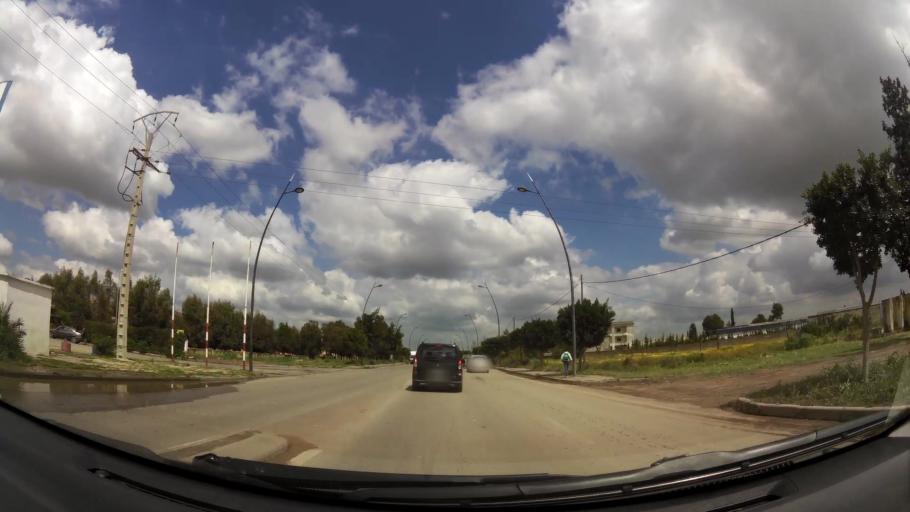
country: MA
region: Chaouia-Ouardigha
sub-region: Settat Province
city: Berrechid
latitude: 33.2618
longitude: -7.6075
